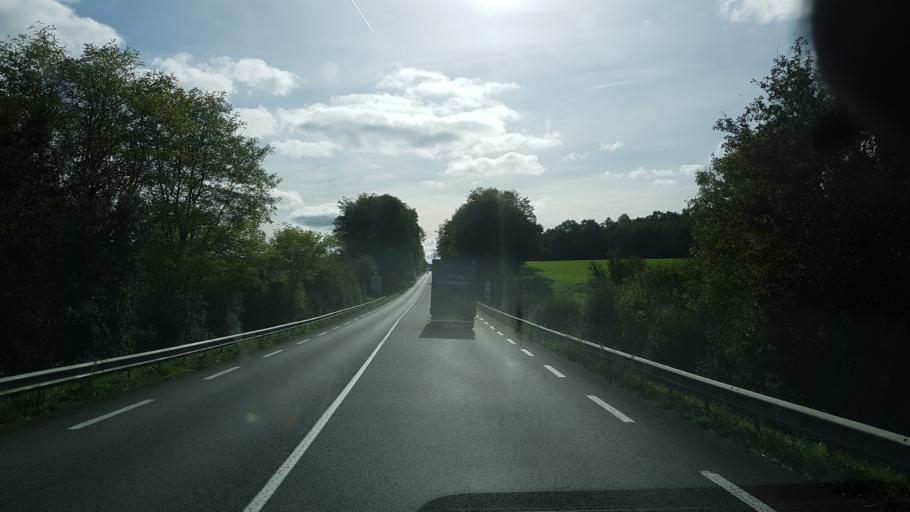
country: FR
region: Poitou-Charentes
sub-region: Departement de la Charente
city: Confolens
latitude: 46.0151
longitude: 0.6455
